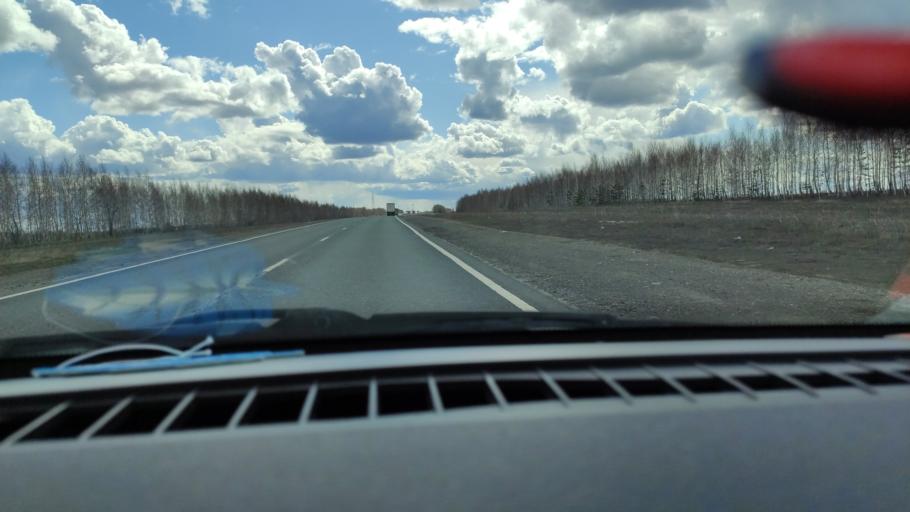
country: RU
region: Saratov
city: Dukhovnitskoye
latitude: 52.8438
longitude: 48.2503
